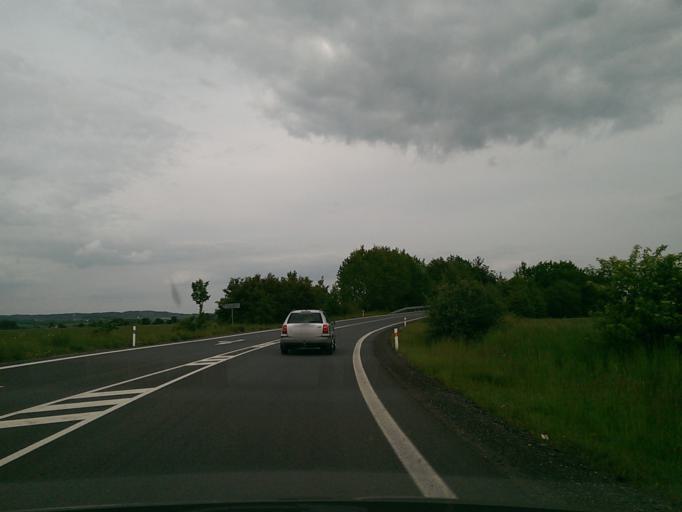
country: CZ
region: Central Bohemia
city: Bakov nad Jizerou
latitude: 50.4860
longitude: 14.9480
